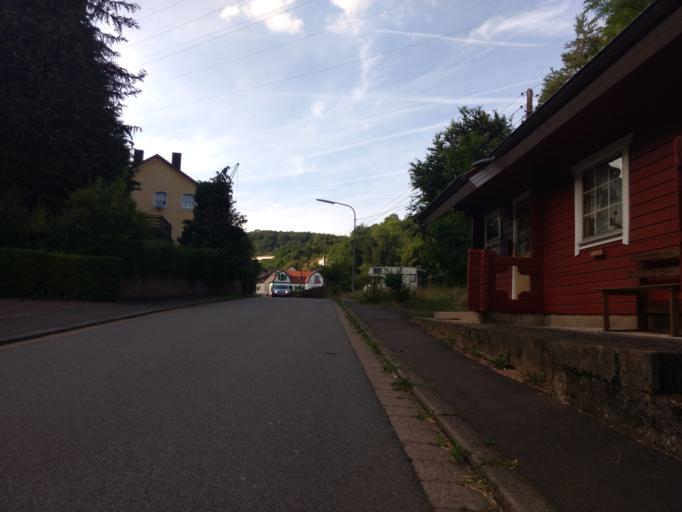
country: DE
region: Saarland
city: Beckingen
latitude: 49.3985
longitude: 6.7002
